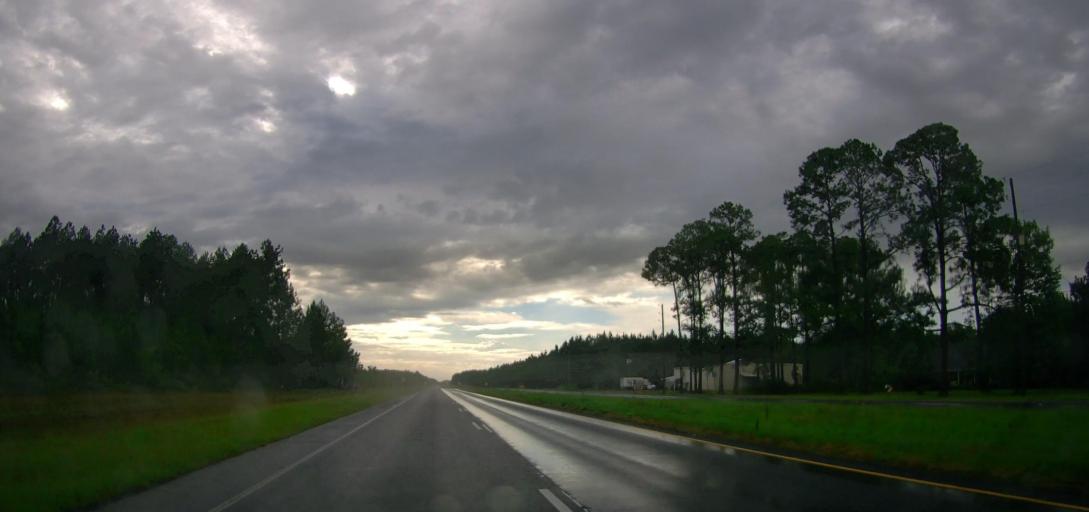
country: US
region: Georgia
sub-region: Ware County
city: Deenwood
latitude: 31.2572
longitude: -82.4952
